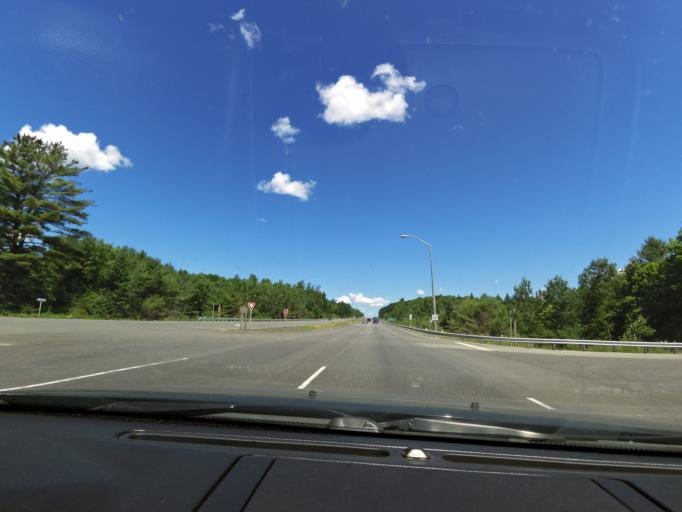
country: CA
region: Ontario
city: Bracebridge
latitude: 45.0908
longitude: -79.3012
